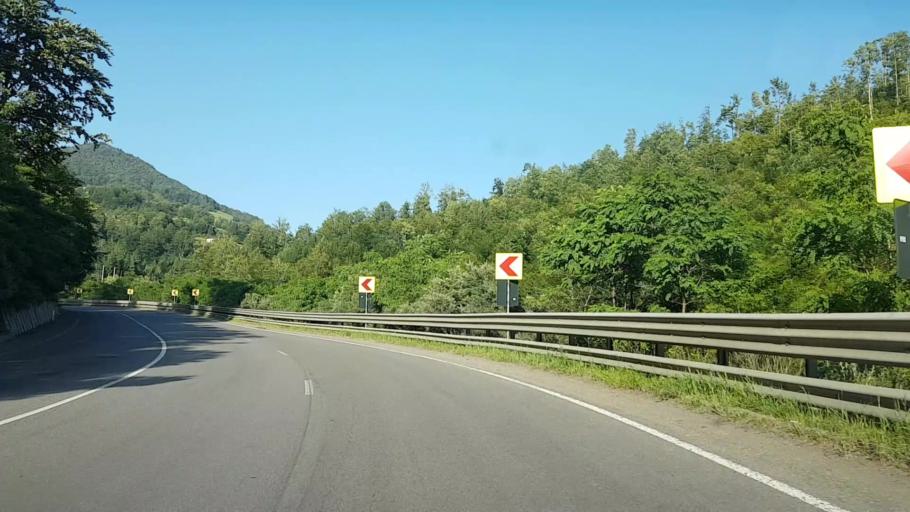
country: RO
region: Bistrita-Nasaud
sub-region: Comuna Tiha Bargaului
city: Tureac
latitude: 47.2219
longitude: 24.9107
